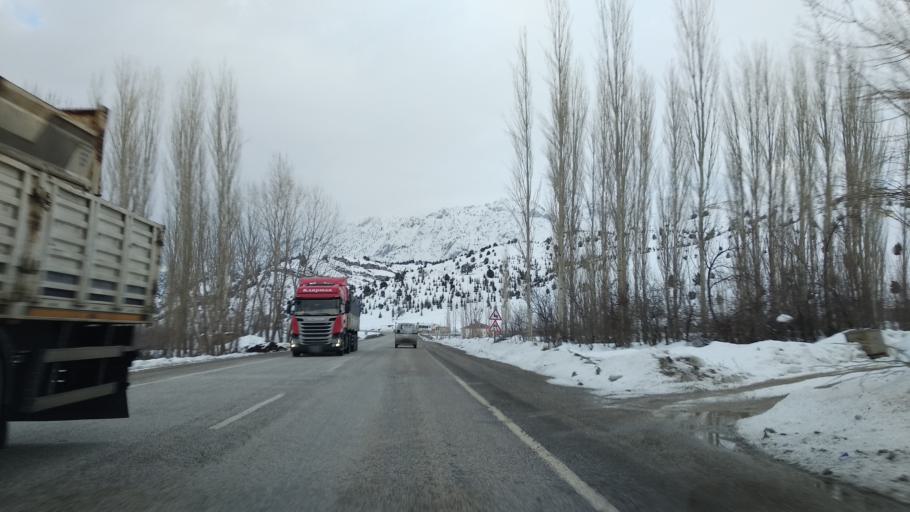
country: TR
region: Kahramanmaras
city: Goksun
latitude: 37.9974
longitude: 36.5273
